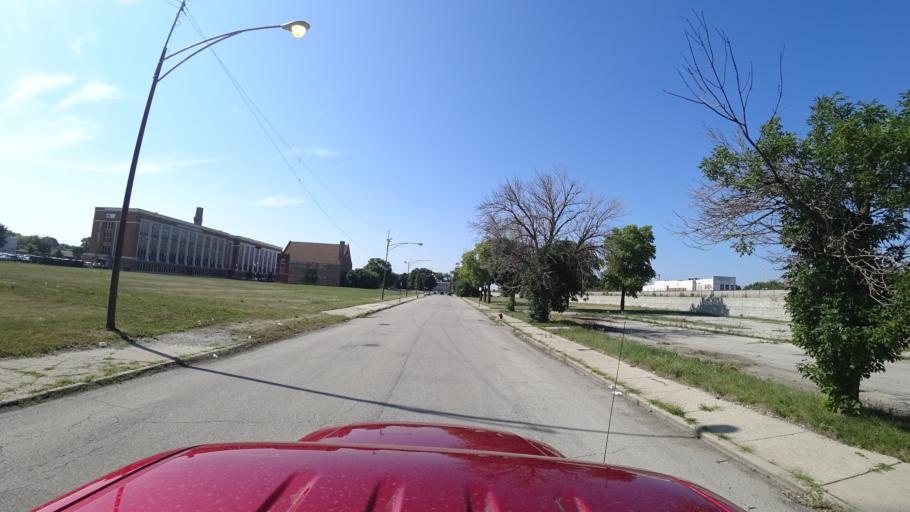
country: US
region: Illinois
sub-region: Cook County
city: Chicago
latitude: 41.8116
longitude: -87.6283
